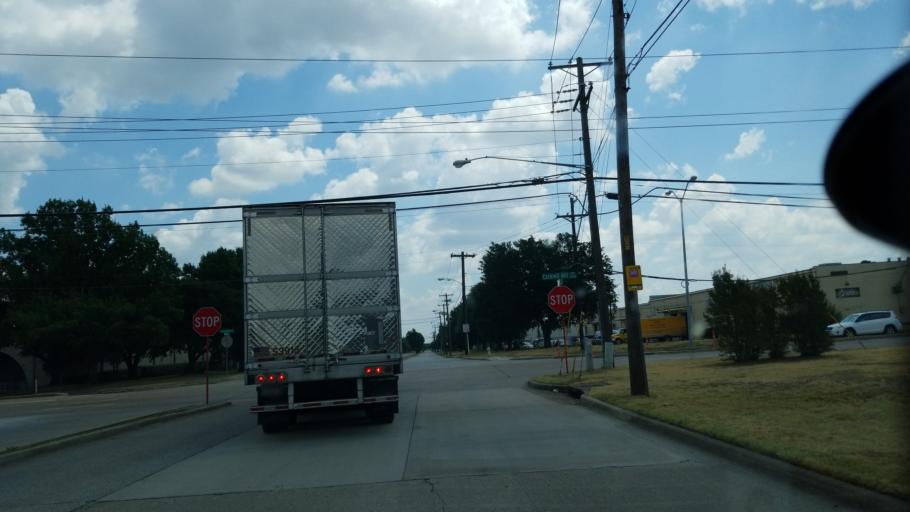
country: US
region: Texas
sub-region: Dallas County
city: Duncanville
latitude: 32.6872
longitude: -96.8919
